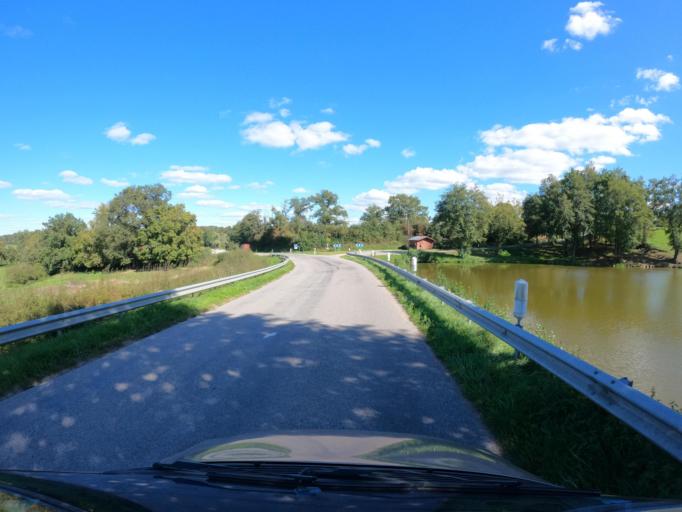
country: FR
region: Auvergne
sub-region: Departement de l'Allier
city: Doyet
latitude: 46.3963
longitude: 2.8666
